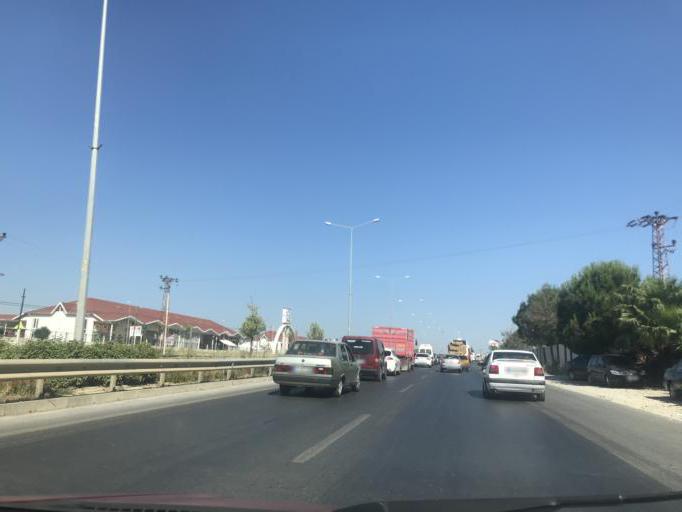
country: TR
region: Antalya
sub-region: Manavgat
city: Side
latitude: 36.8065
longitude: 31.3875
